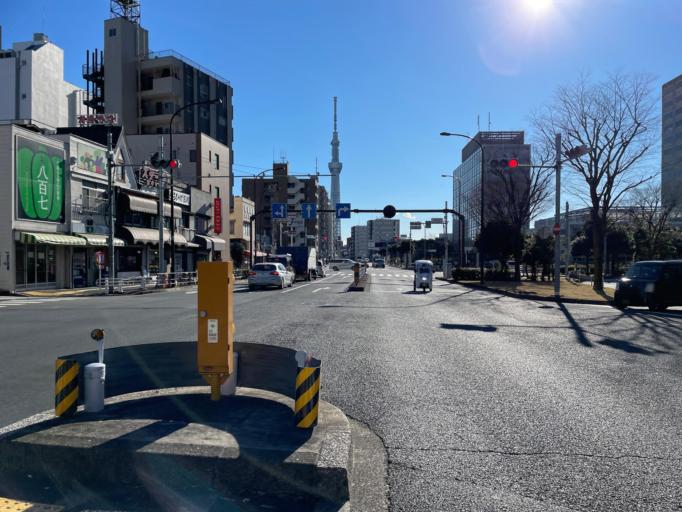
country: JP
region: Saitama
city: Soka
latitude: 35.7282
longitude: 139.8133
